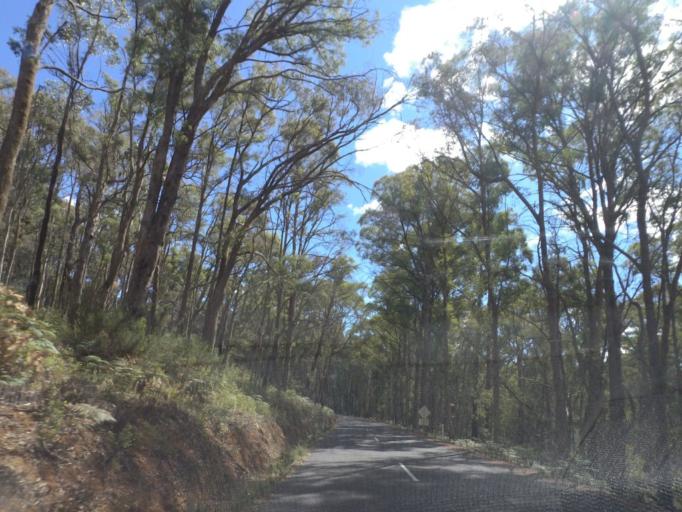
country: AU
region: Victoria
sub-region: Murrindindi
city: Alexandra
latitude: -37.3413
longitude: 145.9652
